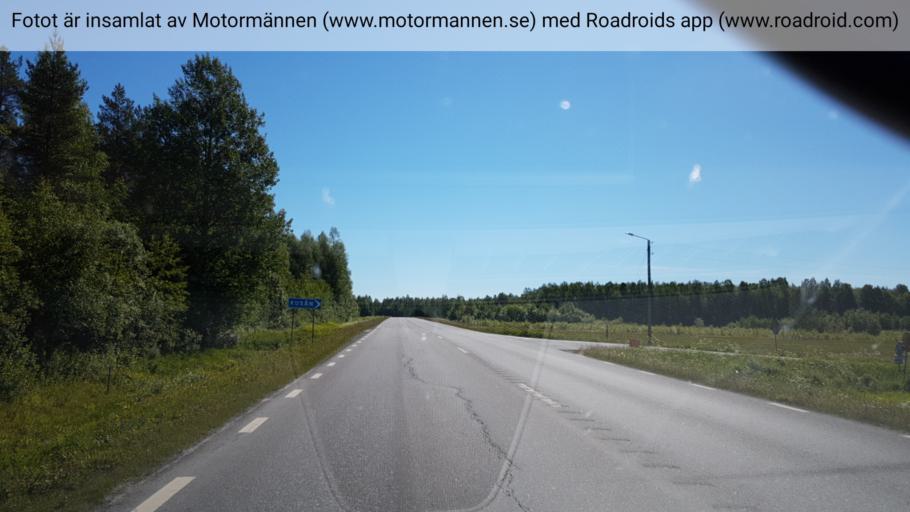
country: SE
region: Norrbotten
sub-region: Bodens Kommun
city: Boden
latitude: 65.8509
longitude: 21.5218
